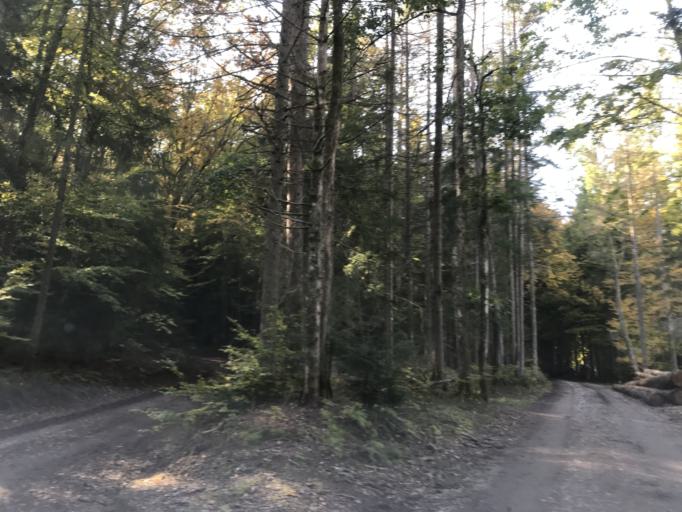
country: DE
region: Baden-Wuerttemberg
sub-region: Freiburg Region
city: Gorwihl
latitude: 47.6362
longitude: 8.0598
